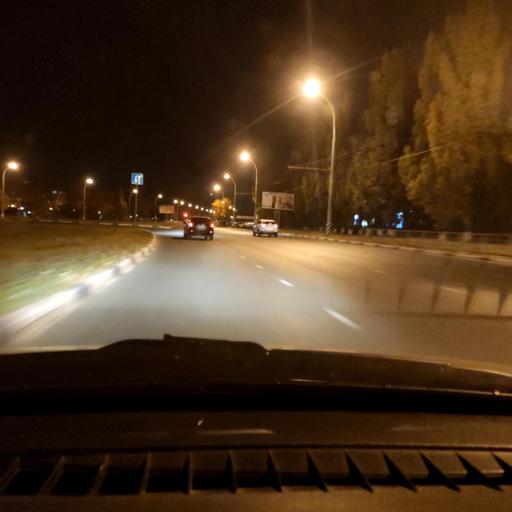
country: RU
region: Samara
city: Tol'yatti
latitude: 53.5194
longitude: 49.2956
